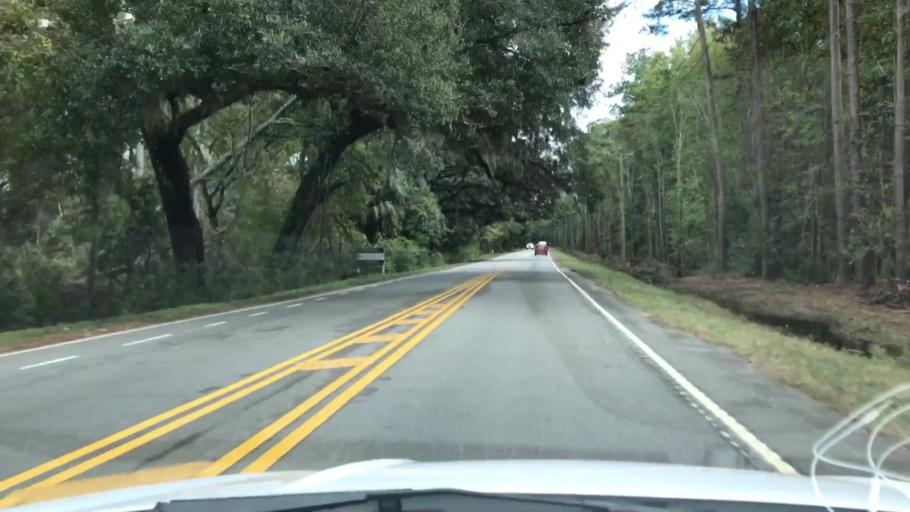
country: US
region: South Carolina
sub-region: Beaufort County
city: Bluffton
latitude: 32.2308
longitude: -80.9190
